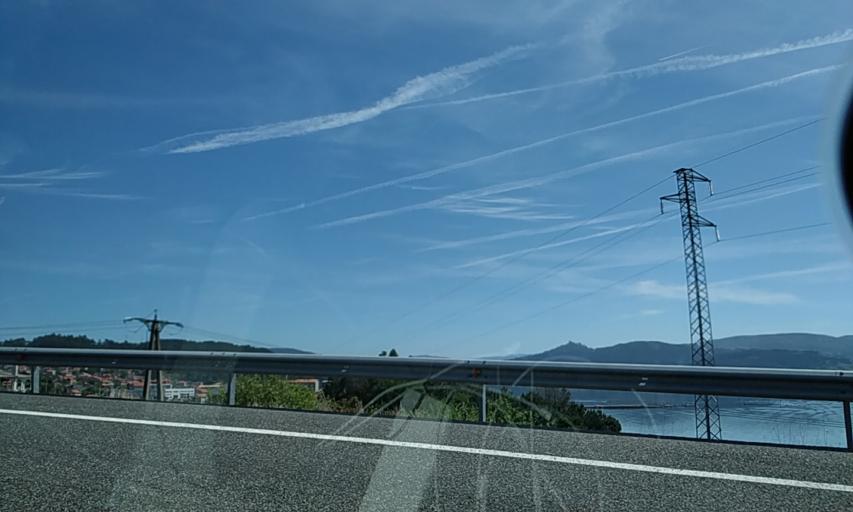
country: ES
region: Galicia
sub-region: Provincia de Pontevedra
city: Redondela
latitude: 42.3180
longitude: -8.6595
